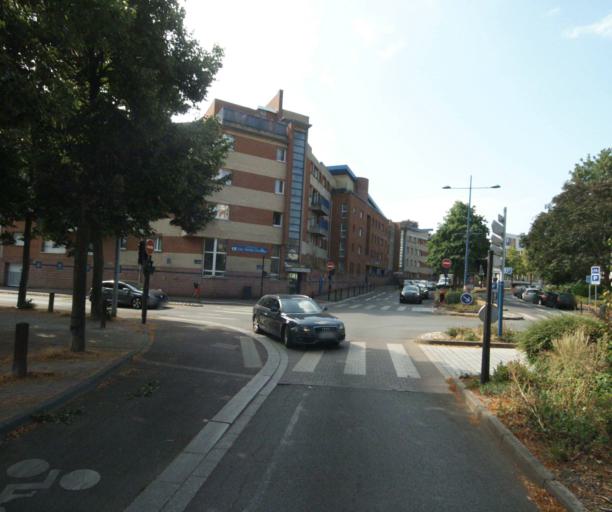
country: FR
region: Nord-Pas-de-Calais
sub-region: Departement du Nord
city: Tourcoing
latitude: 50.7225
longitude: 3.1643
